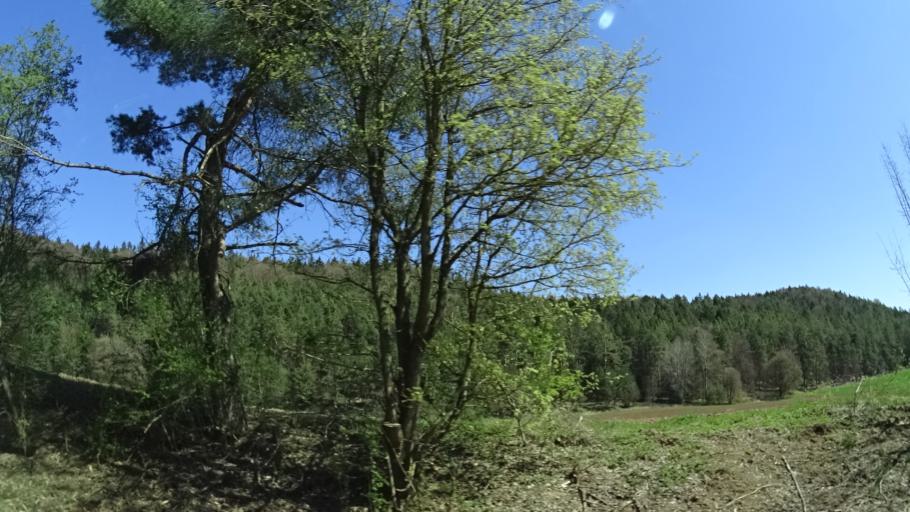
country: DE
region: Bavaria
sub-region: Upper Palatinate
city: Illschwang
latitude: 49.4139
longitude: 11.6864
